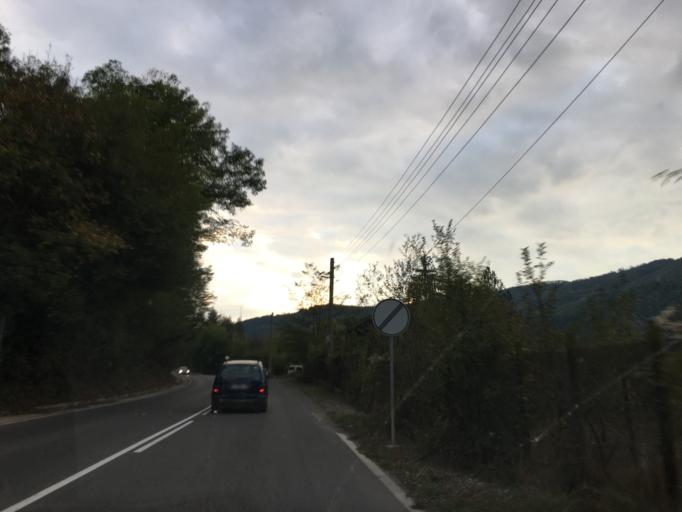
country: BG
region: Sofiya
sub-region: Obshtina Svoge
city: Svoge
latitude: 42.9325
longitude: 23.3881
